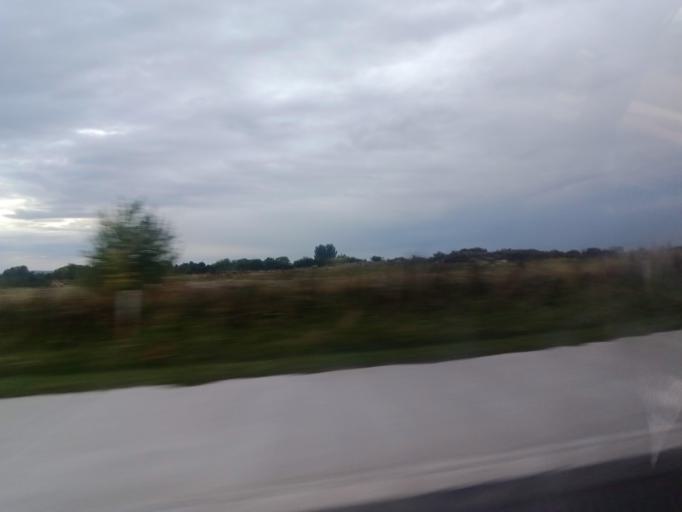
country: IE
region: Leinster
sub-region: Laois
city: Portlaoise
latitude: 53.0170
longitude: -7.3157
